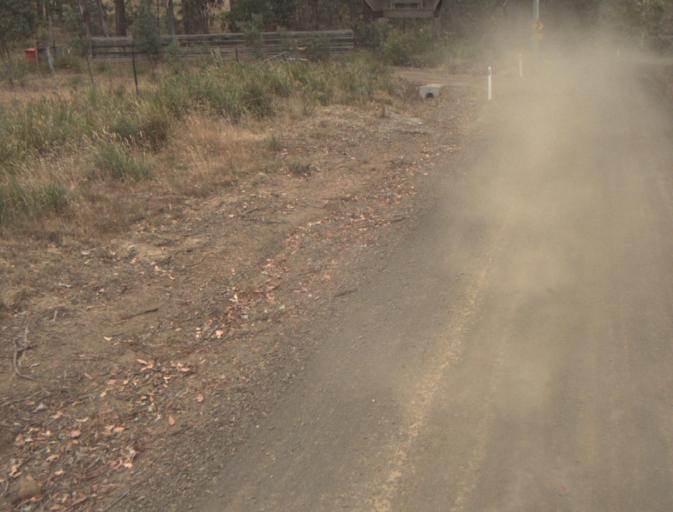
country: AU
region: Tasmania
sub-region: Northern Midlands
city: Evandale
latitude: -41.5210
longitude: 147.4387
